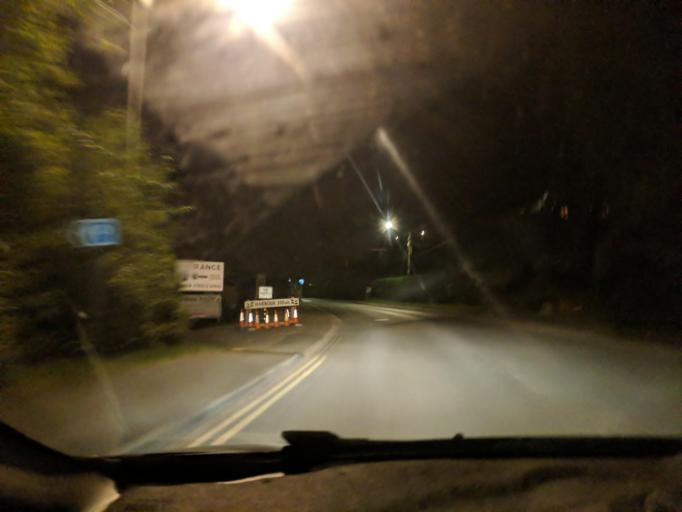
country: GB
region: England
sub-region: Cornwall
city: Mevagissey
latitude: 50.2717
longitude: -4.7907
